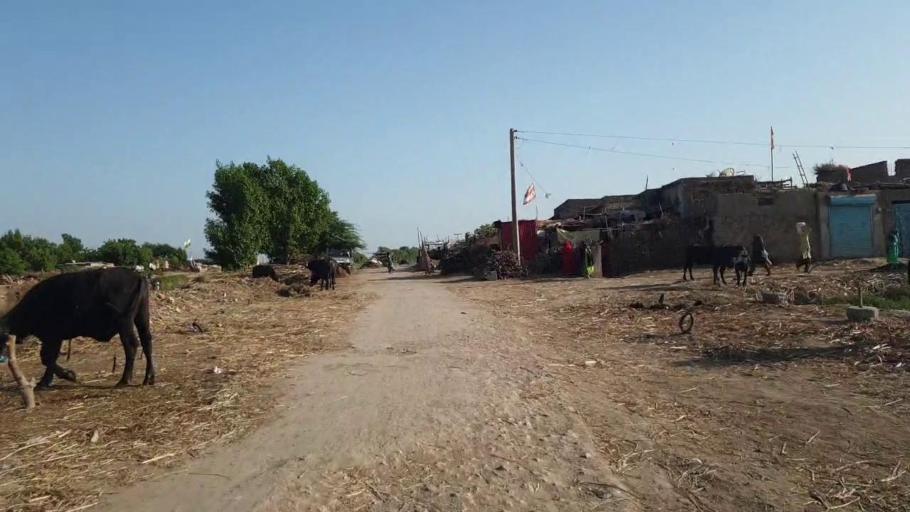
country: PK
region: Sindh
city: Hyderabad
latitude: 25.3240
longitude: 68.4264
